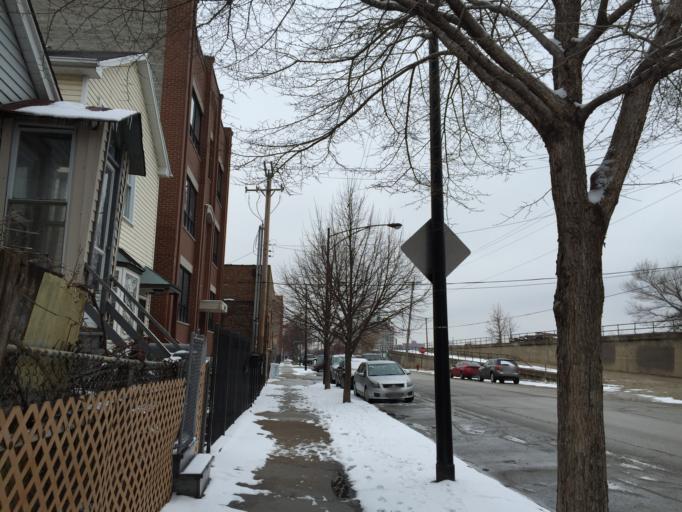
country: US
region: Illinois
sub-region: Cook County
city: Chicago
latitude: 41.8598
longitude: -87.6512
